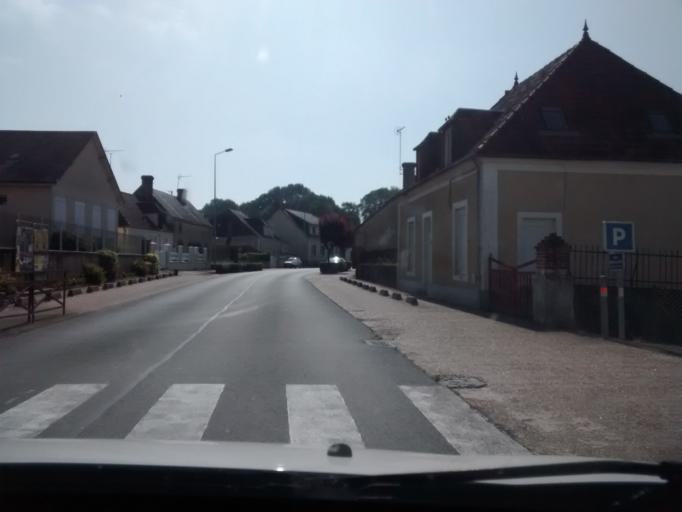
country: FR
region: Pays de la Loire
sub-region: Departement de la Sarthe
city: Vibraye
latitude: 48.1159
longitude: 0.7054
